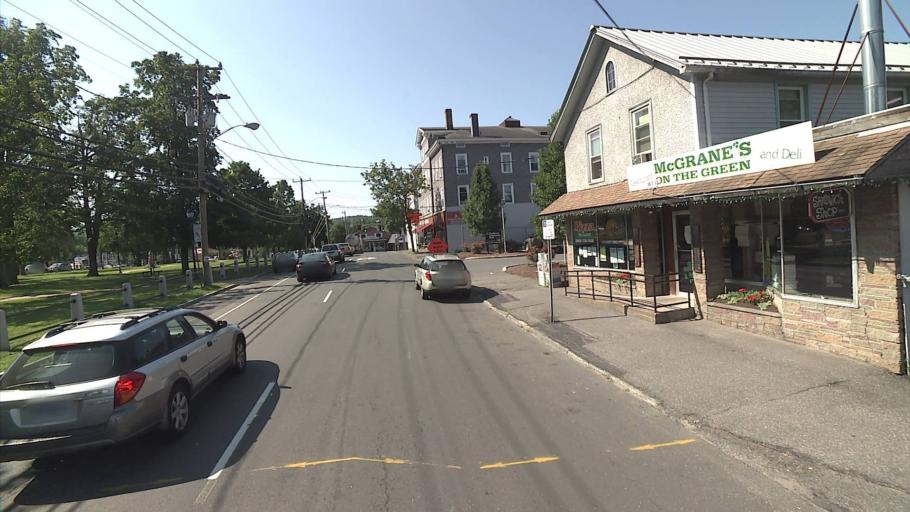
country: US
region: Connecticut
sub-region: Litchfield County
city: Winsted
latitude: 41.9220
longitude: -73.0604
